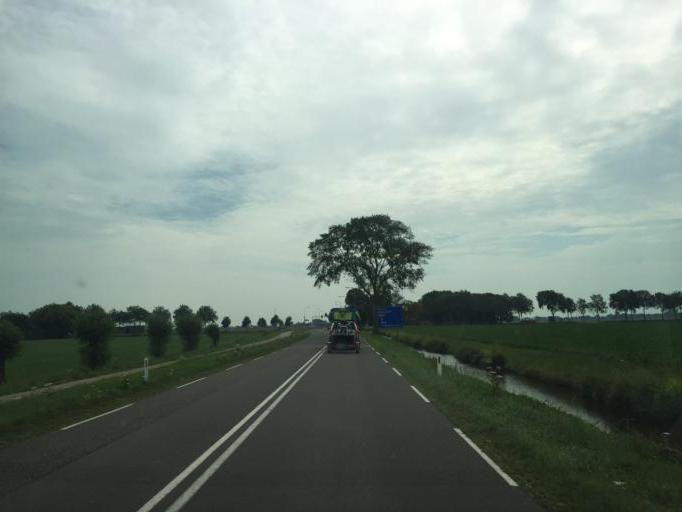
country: NL
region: North Holland
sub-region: Gemeente Beemster
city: Halfweg
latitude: 52.5945
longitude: 4.9071
